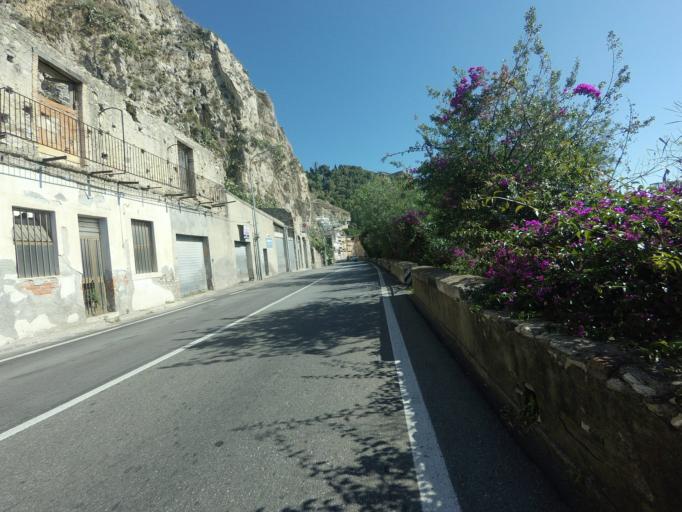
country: IT
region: Sicily
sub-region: Messina
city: Taormina
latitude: 37.8475
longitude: 15.2844
